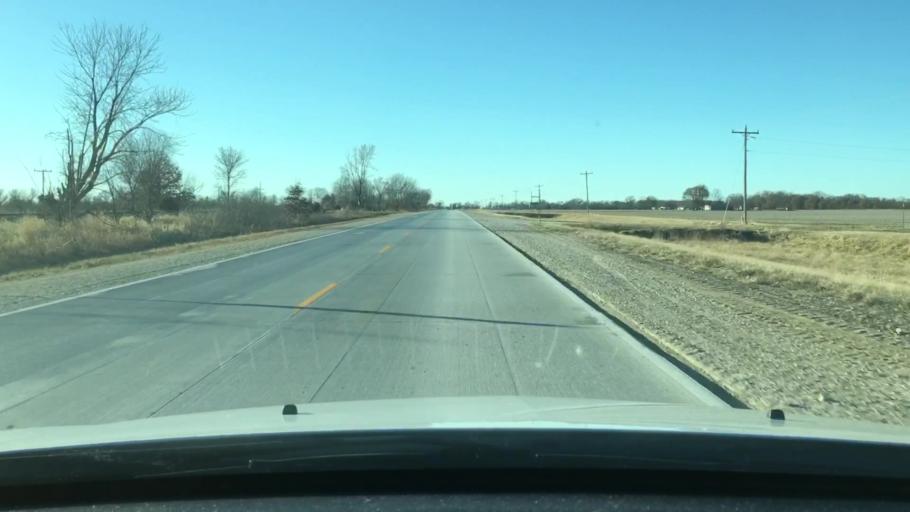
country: US
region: Missouri
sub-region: Boone County
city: Centralia
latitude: 39.1925
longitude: -92.0136
